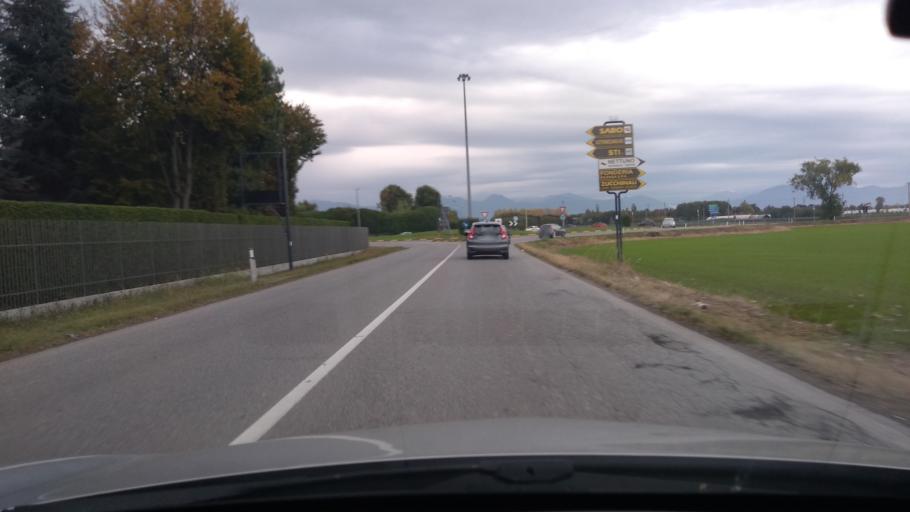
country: IT
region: Lombardy
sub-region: Provincia di Bergamo
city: Levate
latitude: 45.6189
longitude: 9.6344
